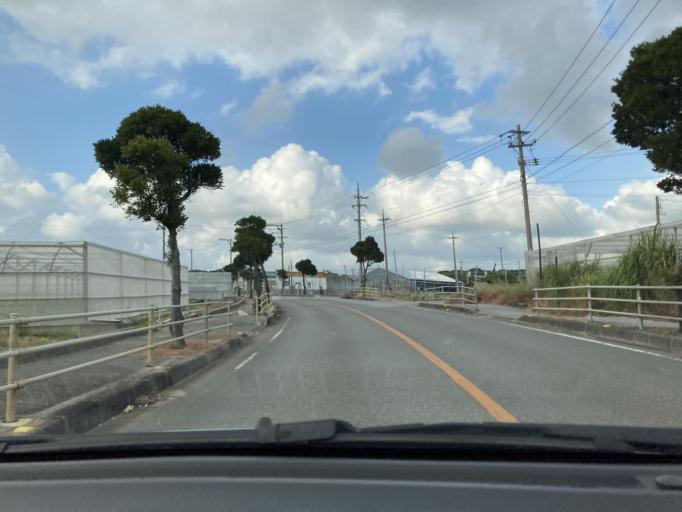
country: JP
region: Okinawa
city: Itoman
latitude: 26.1026
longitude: 127.6669
